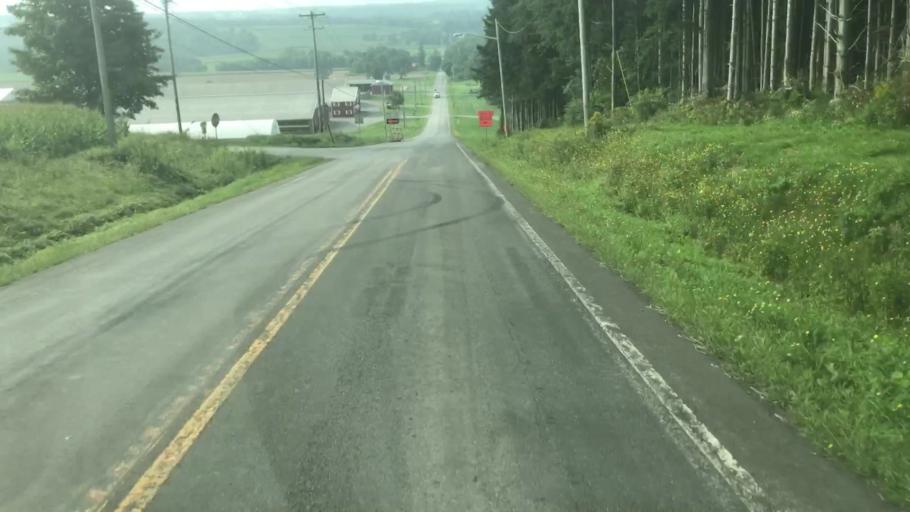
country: US
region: New York
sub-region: Onondaga County
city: Skaneateles
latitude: 42.8650
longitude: -76.4485
